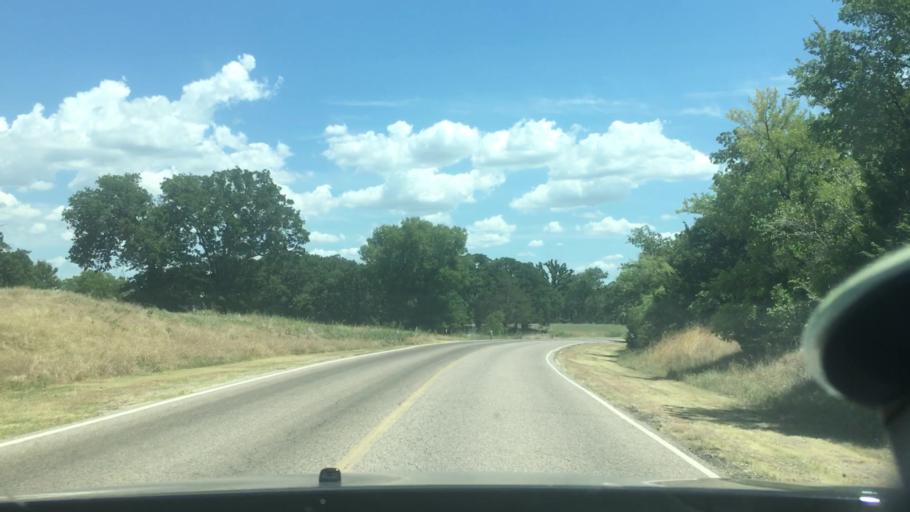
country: US
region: Oklahoma
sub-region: Marshall County
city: Kingston
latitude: 33.9915
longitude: -96.6400
